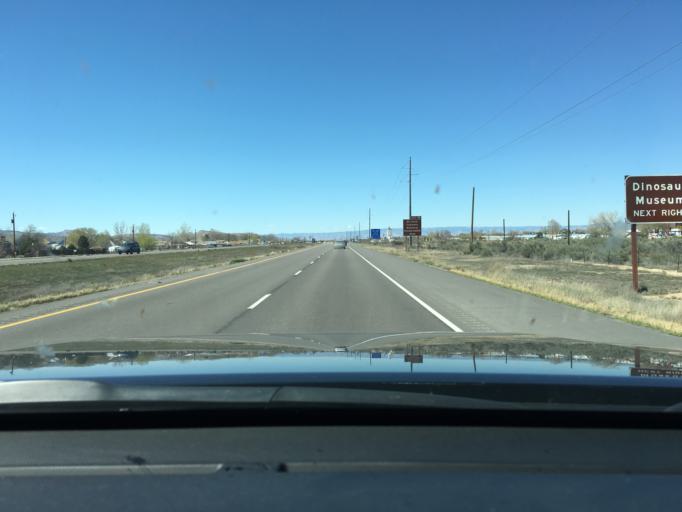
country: US
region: Colorado
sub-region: Mesa County
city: Fruita
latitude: 39.1469
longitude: -108.7188
